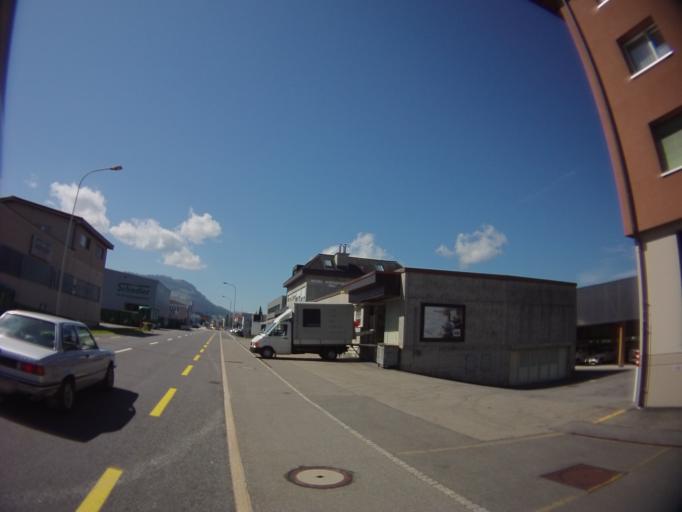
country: CH
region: Schwyz
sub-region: Bezirk Einsiedeln
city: Einsiedeln
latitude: 47.1371
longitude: 8.7457
